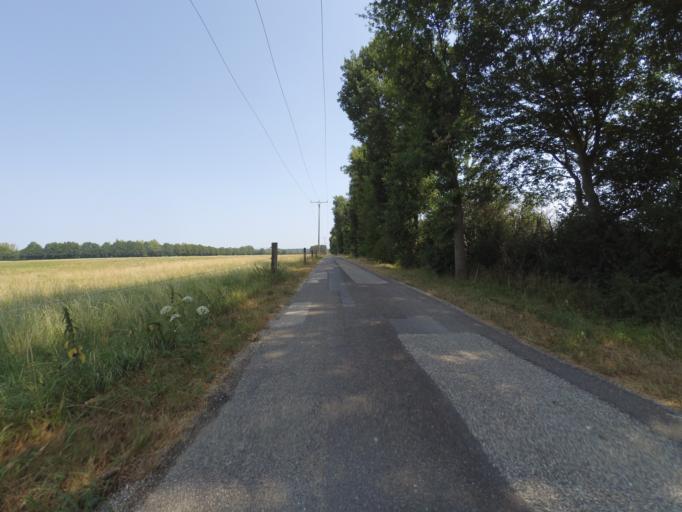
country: DE
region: North Rhine-Westphalia
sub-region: Regierungsbezirk Dusseldorf
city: Mehrhoog
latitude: 51.7430
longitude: 6.4671
